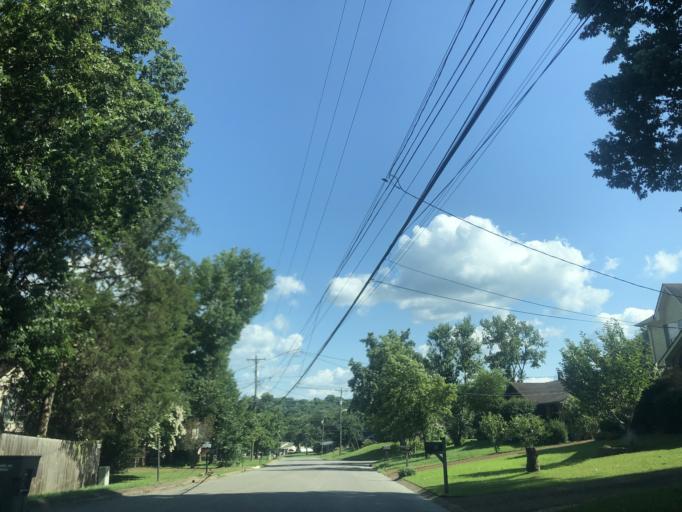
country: US
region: Tennessee
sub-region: Davidson County
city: Lakewood
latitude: 36.2005
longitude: -86.6016
